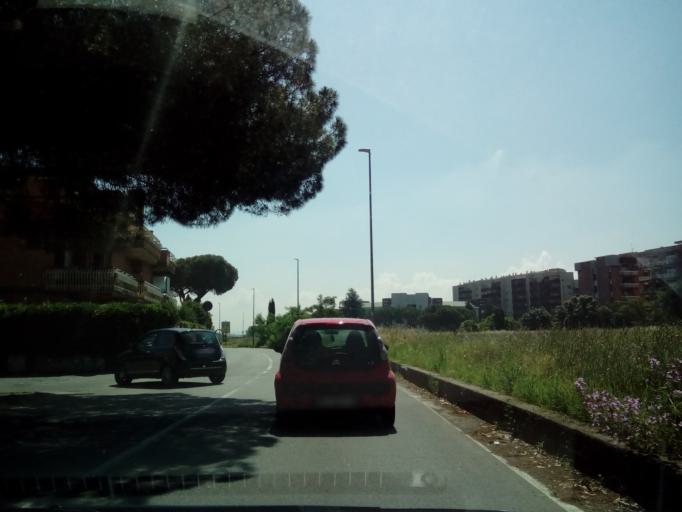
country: IT
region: Latium
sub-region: Citta metropolitana di Roma Capitale
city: Rome
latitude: 41.8912
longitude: 12.5852
